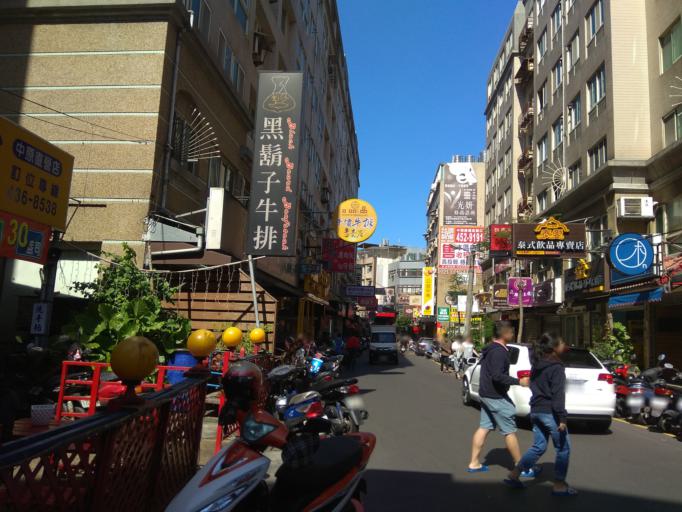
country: TW
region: Taiwan
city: Taoyuan City
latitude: 24.9575
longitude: 121.2392
